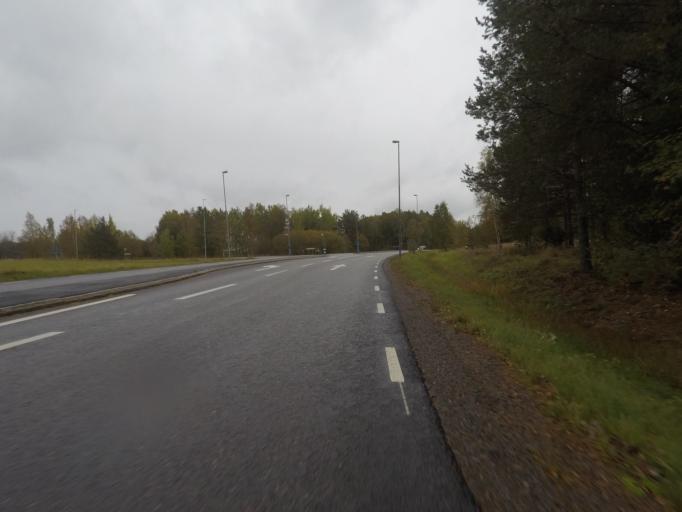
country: SE
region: OErebro
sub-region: Karlskoga Kommun
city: Karlskoga
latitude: 59.3165
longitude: 14.4724
